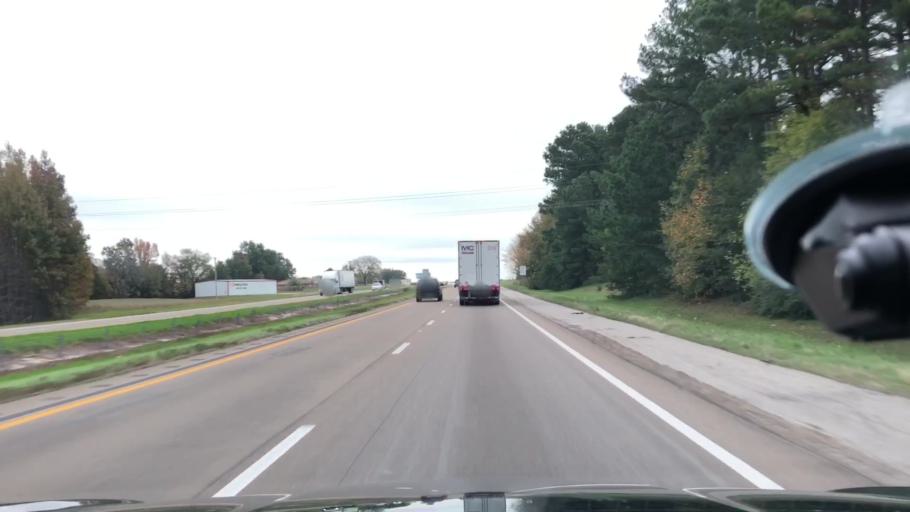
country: US
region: Texas
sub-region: Titus County
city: Mount Pleasant
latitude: 33.1604
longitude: -95.0294
